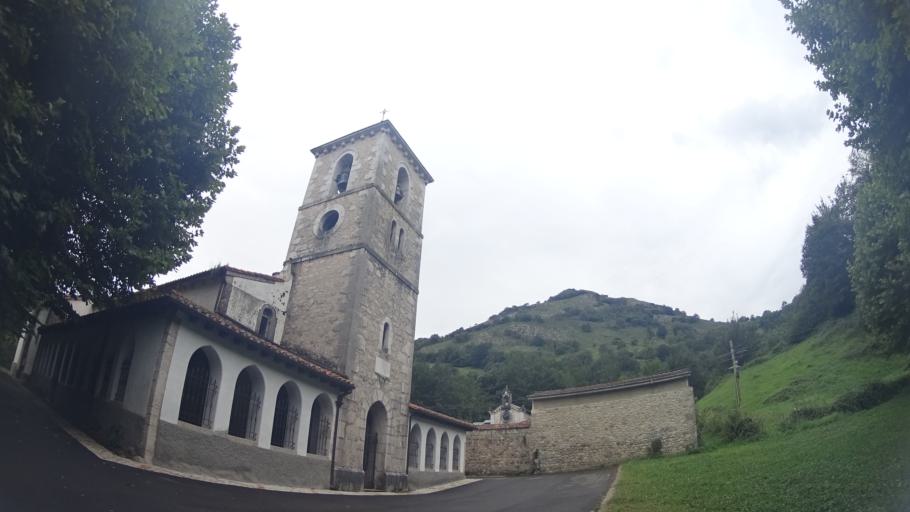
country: ES
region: Asturias
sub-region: Province of Asturias
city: Carrena
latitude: 43.3345
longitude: -4.9728
